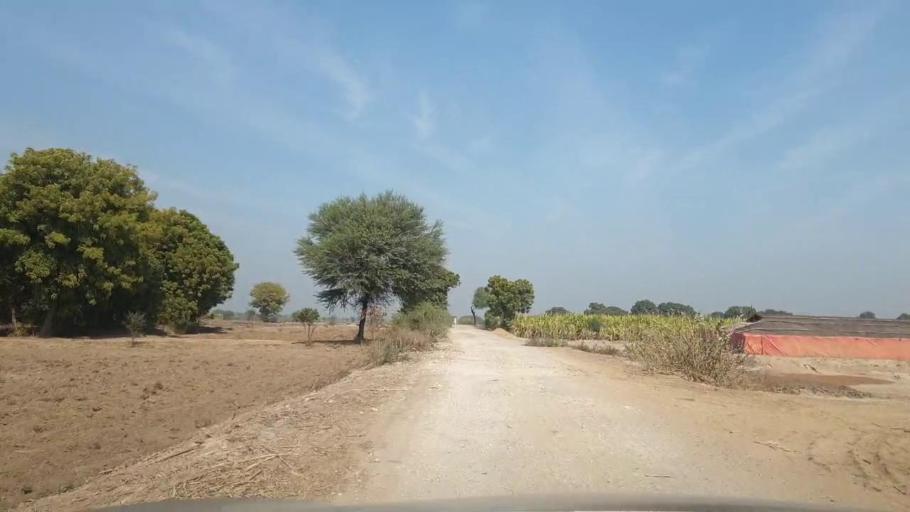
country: PK
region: Sindh
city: Tando Adam
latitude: 25.6422
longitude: 68.7284
